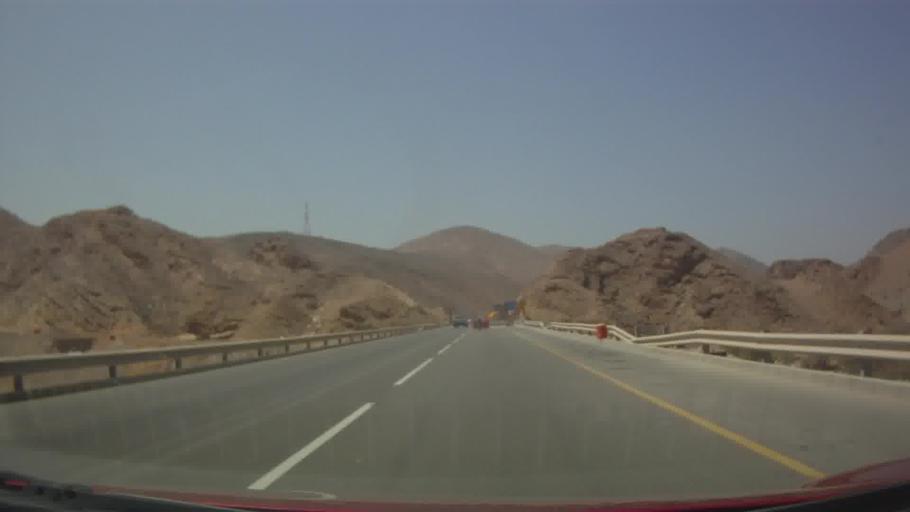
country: OM
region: Muhafazat Masqat
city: Muscat
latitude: 23.5239
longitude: 58.6378
